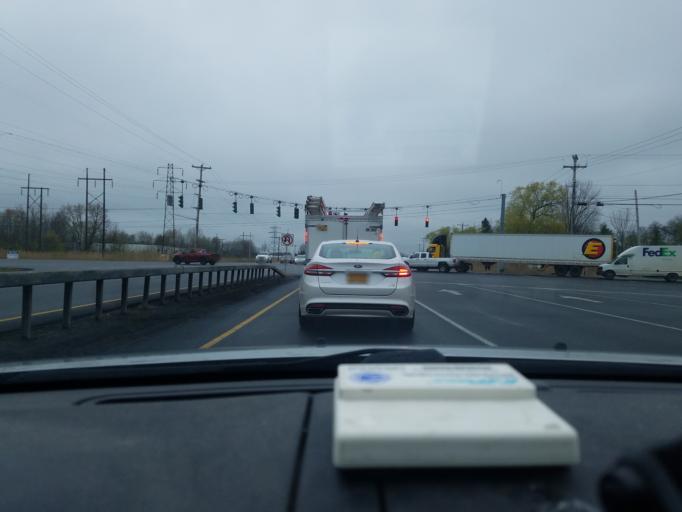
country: US
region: New York
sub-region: Onondaga County
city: North Syracuse
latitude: 43.1276
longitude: -76.0795
